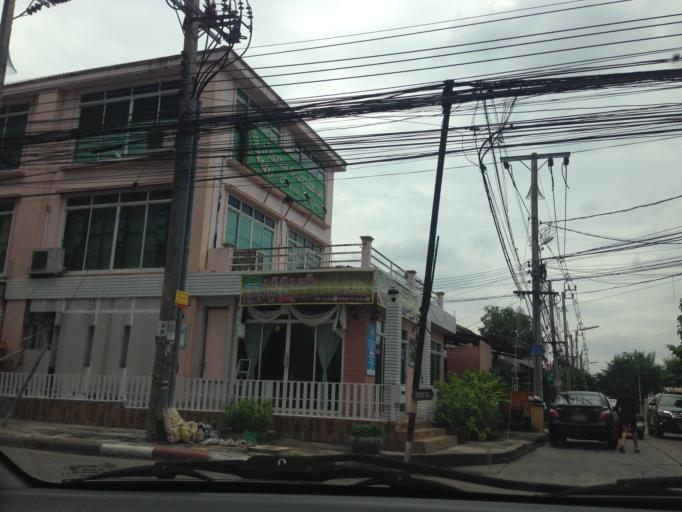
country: TH
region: Nonthaburi
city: Pak Kret
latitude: 13.9251
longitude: 100.5345
